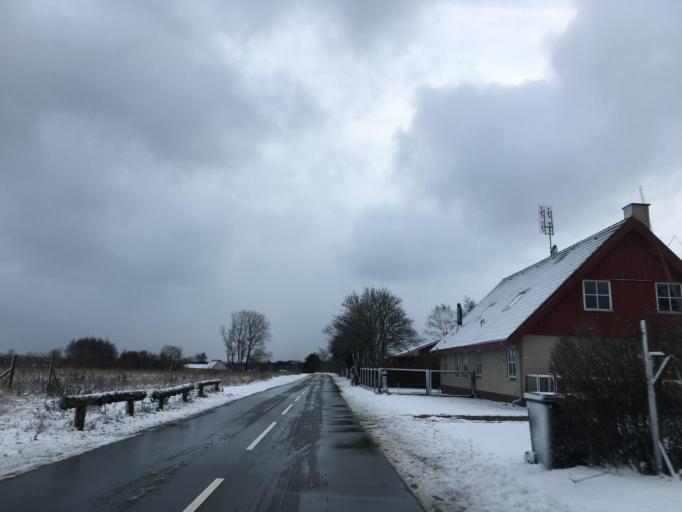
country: DK
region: Zealand
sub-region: Odsherred Kommune
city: Asnaes
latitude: 55.8366
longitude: 11.5567
